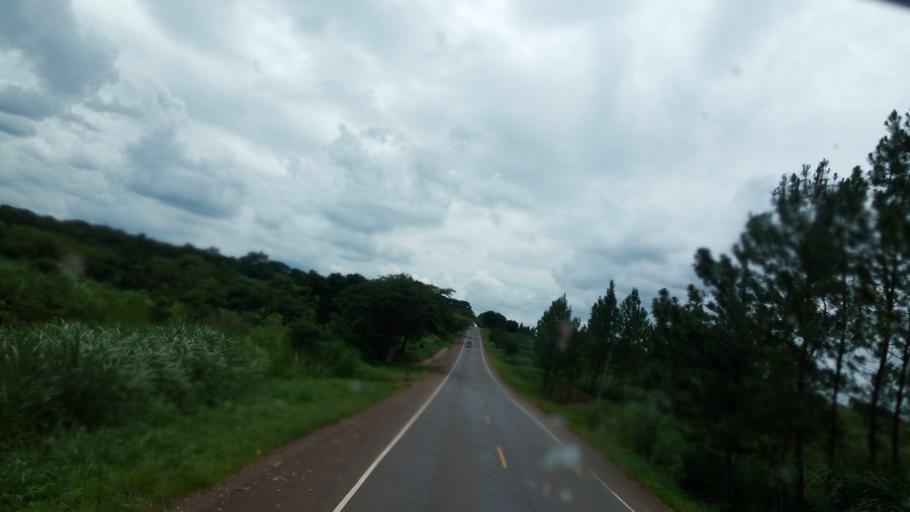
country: UG
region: Western Region
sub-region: Kiryandongo District
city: Kiryandongo
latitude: 2.0646
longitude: 32.1896
